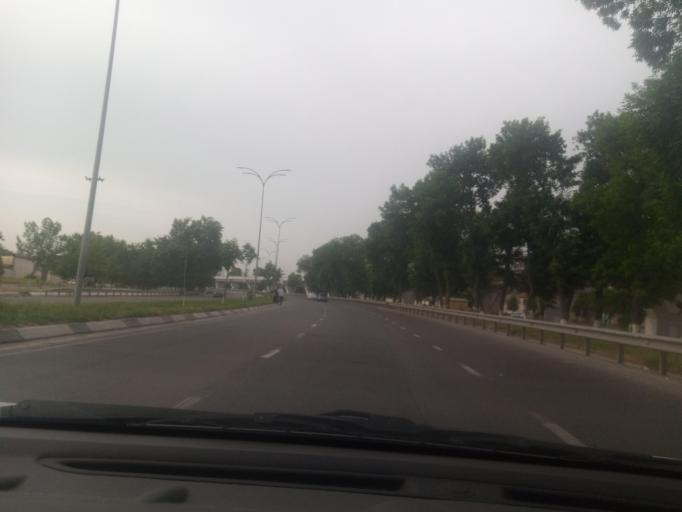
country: UZ
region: Toshkent Shahri
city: Bektemir
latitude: 41.2728
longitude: 69.3622
